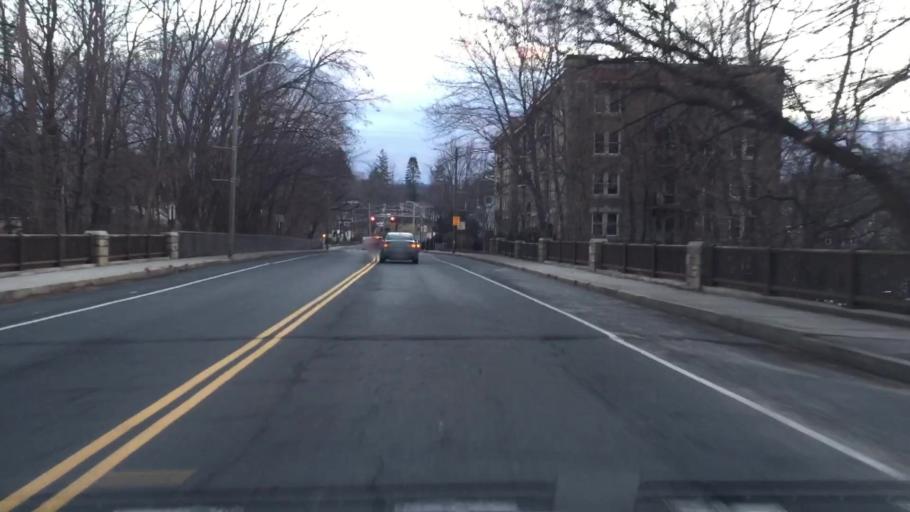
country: US
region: Massachusetts
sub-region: Hampshire County
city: Northampton
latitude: 42.3164
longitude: -72.6337
